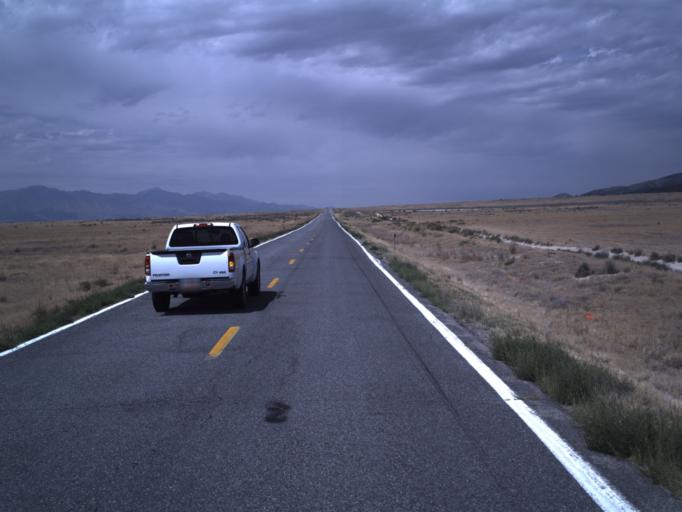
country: US
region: Utah
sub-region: Utah County
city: Eagle Mountain
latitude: 40.2438
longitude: -112.2091
